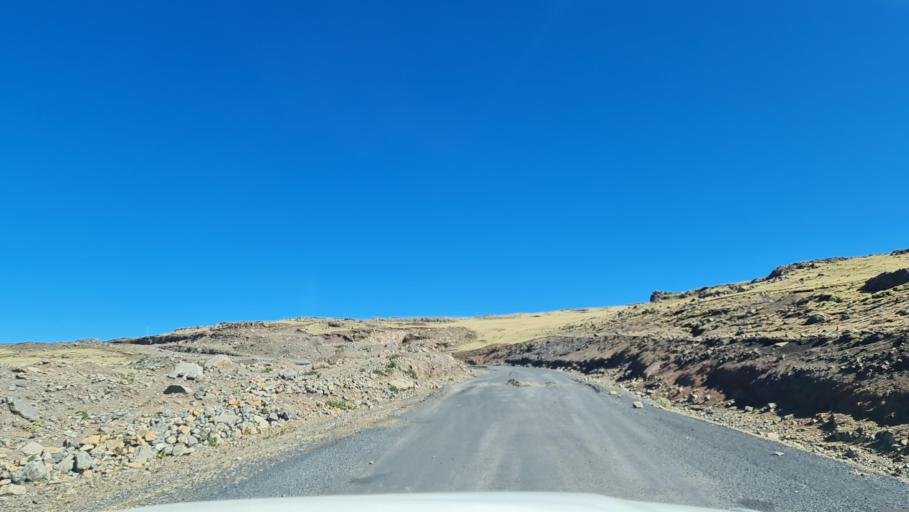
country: ET
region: Amhara
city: Debark'
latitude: 13.1508
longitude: 38.1876
